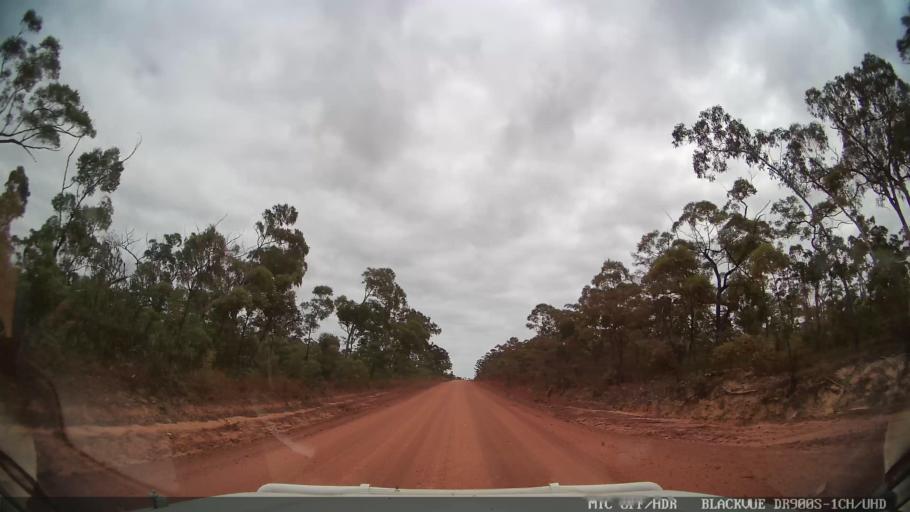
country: AU
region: Queensland
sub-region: Cook
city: Cooktown
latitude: -15.2666
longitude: 144.9471
